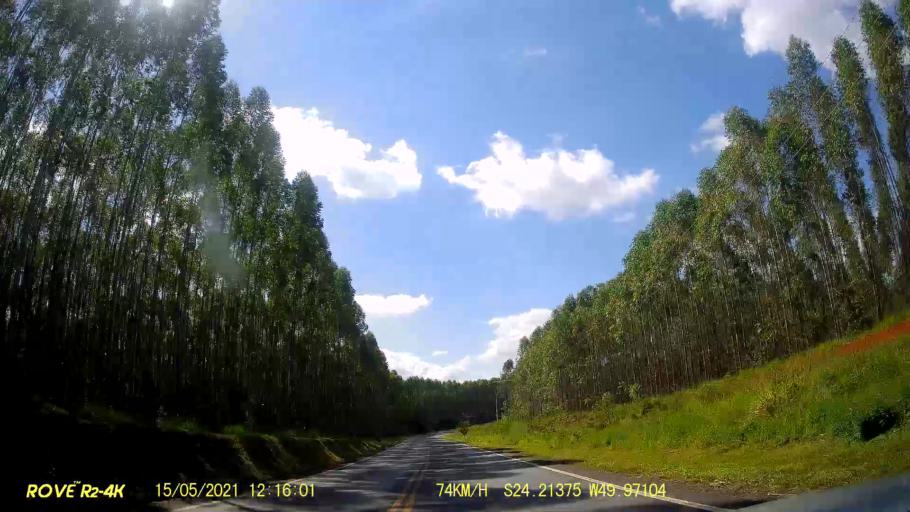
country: BR
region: Parana
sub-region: Jaguariaiva
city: Jaguariaiva
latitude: -24.2138
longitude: -49.9712
